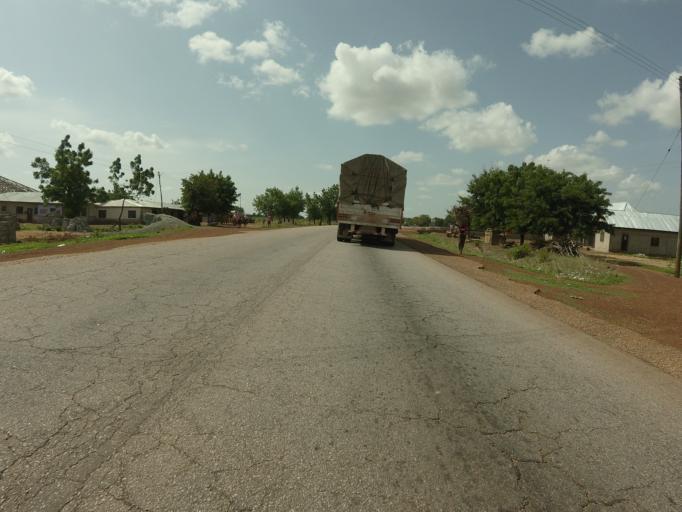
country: GH
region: Northern
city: Savelugu
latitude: 9.8754
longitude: -0.8722
